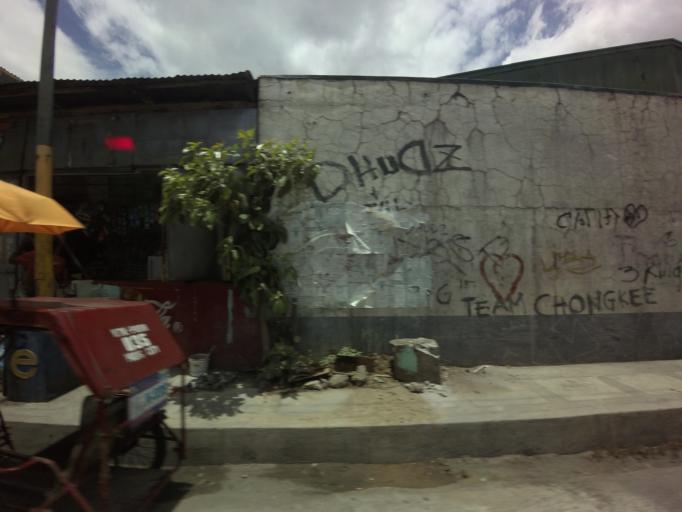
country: PH
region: Metro Manila
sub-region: Marikina
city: Calumpang
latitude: 14.6064
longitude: 121.1040
